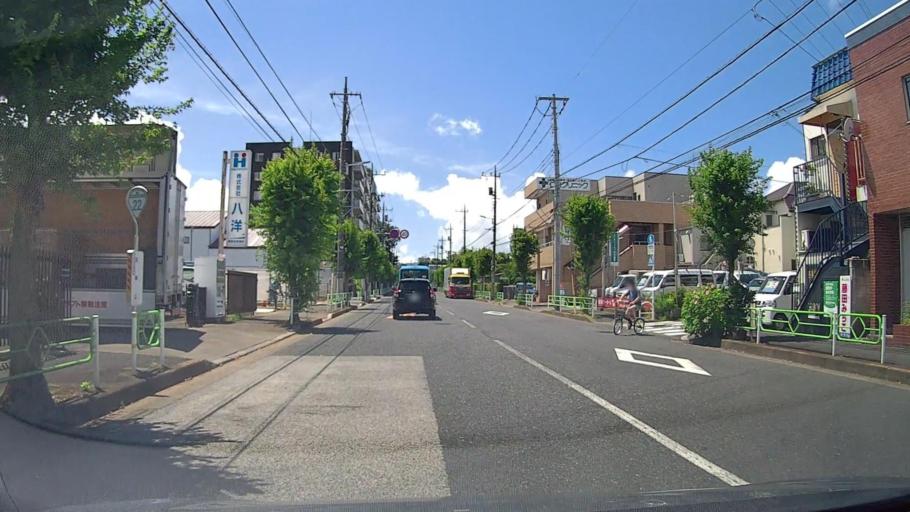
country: JP
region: Tokyo
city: Nishi-Tokyo-shi
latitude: 35.7372
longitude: 139.5659
